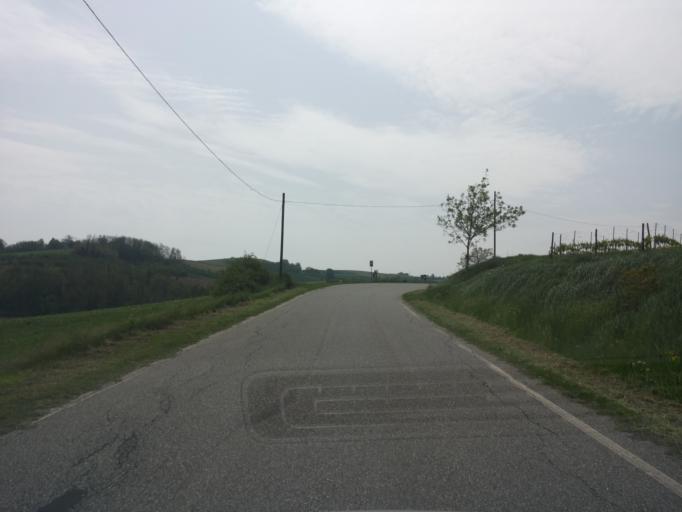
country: IT
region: Piedmont
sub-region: Provincia di Alessandria
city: Mirabello Monferrato
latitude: 45.0155
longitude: 8.5109
